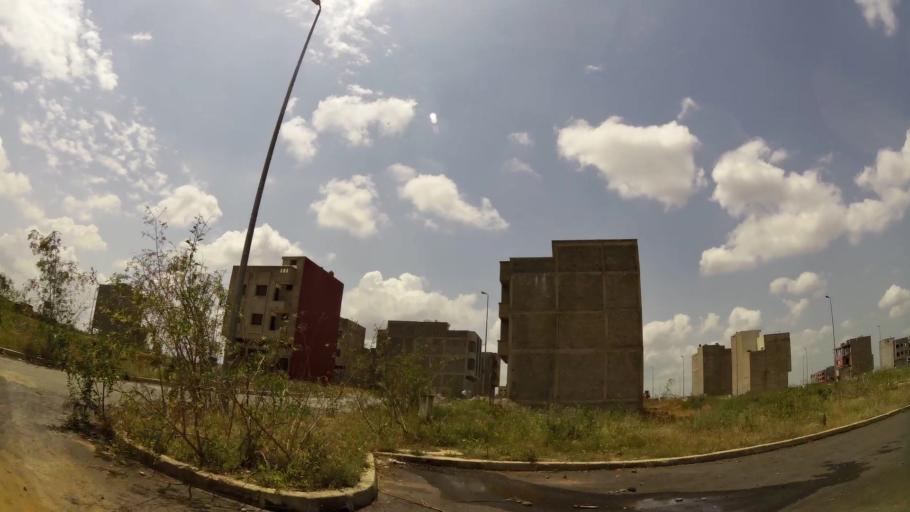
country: MA
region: Rabat-Sale-Zemmour-Zaer
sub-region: Khemisset
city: Tiflet
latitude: 34.0002
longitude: -6.5370
